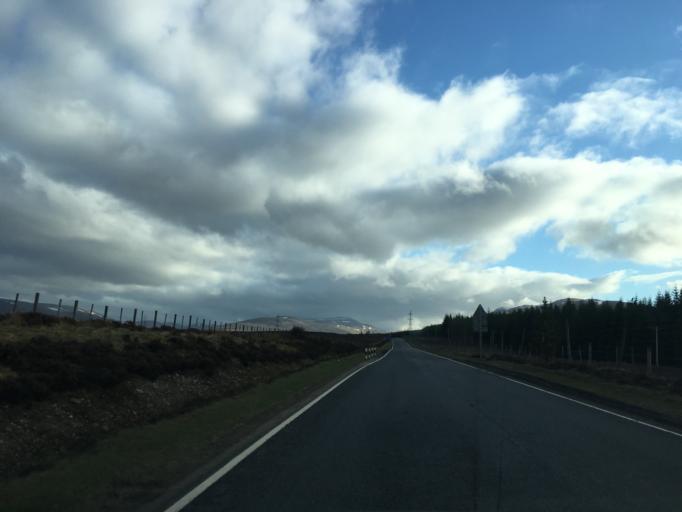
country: GB
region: Scotland
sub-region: Highland
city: Kingussie
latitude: 56.9710
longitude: -4.2360
